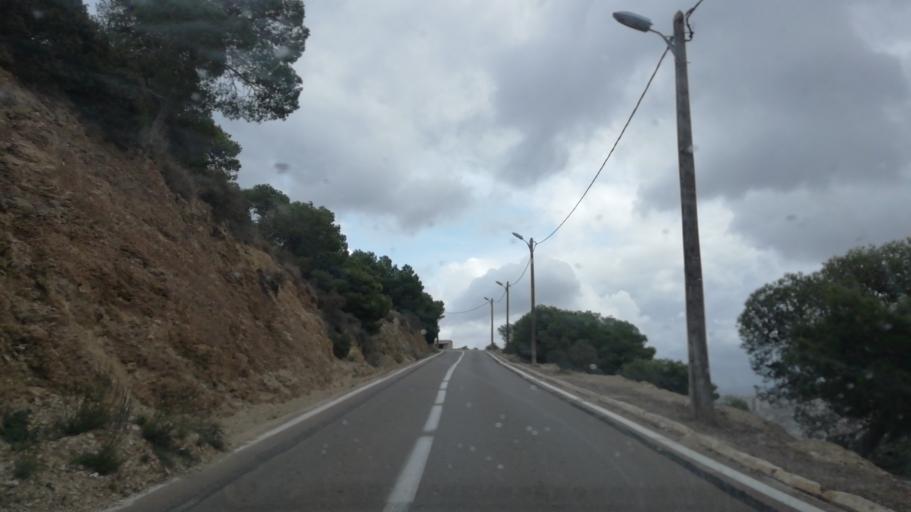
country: DZ
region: Oran
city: Oran
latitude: 35.7070
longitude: -0.6637
